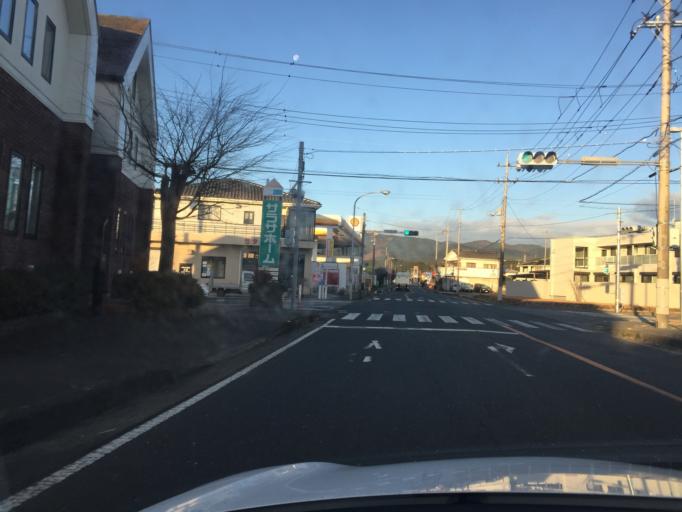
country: JP
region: Ibaraki
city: Kitaibaraki
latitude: 36.7916
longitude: 140.7358
